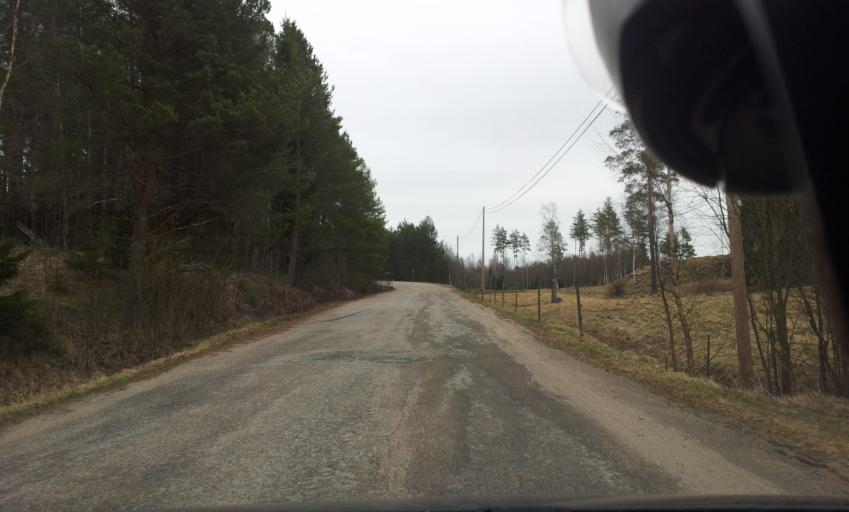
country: SE
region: Gaevleborg
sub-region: Ljusdals Kommun
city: Farila
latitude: 61.8065
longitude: 15.9354
